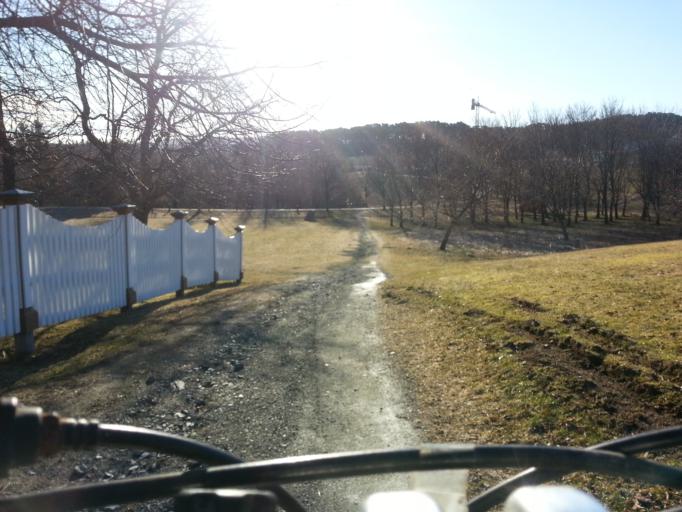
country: NO
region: Sor-Trondelag
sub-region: Trondheim
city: Trondheim
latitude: 63.4385
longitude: 10.4694
